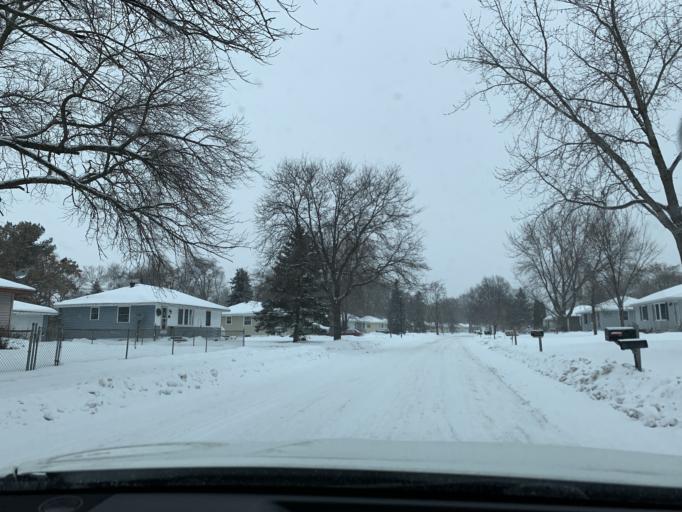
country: US
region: Minnesota
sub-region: Anoka County
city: Blaine
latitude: 45.1751
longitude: -93.2868
